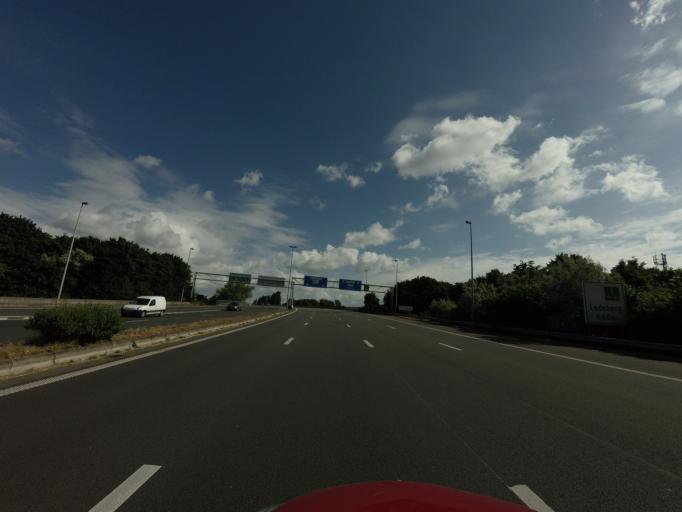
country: BE
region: Flanders
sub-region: Provincie Oost-Vlaanderen
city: Ledeberg
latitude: 51.0302
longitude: 3.7395
